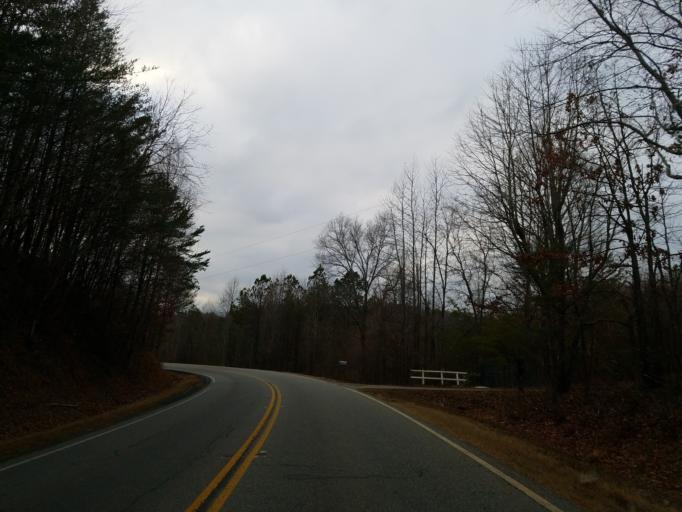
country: US
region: Georgia
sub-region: Bartow County
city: Rydal
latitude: 34.3490
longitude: -84.6541
